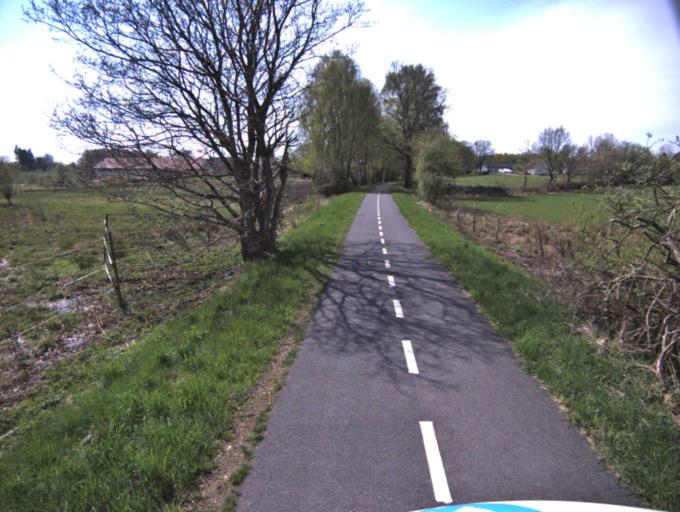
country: SE
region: Skane
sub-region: Kristianstads Kommun
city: Onnestad
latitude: 56.0008
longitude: 14.0444
